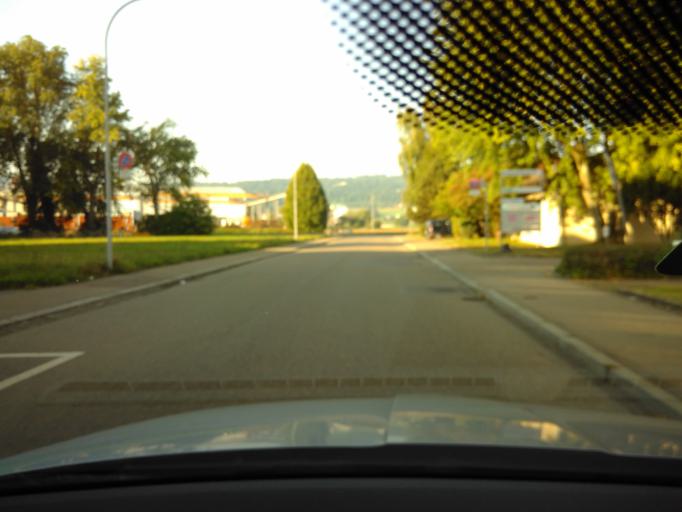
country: CH
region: Zurich
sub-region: Bezirk Dielsdorf
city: Regensdorf / Hofacher-Geeren
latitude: 47.4440
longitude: 8.4594
